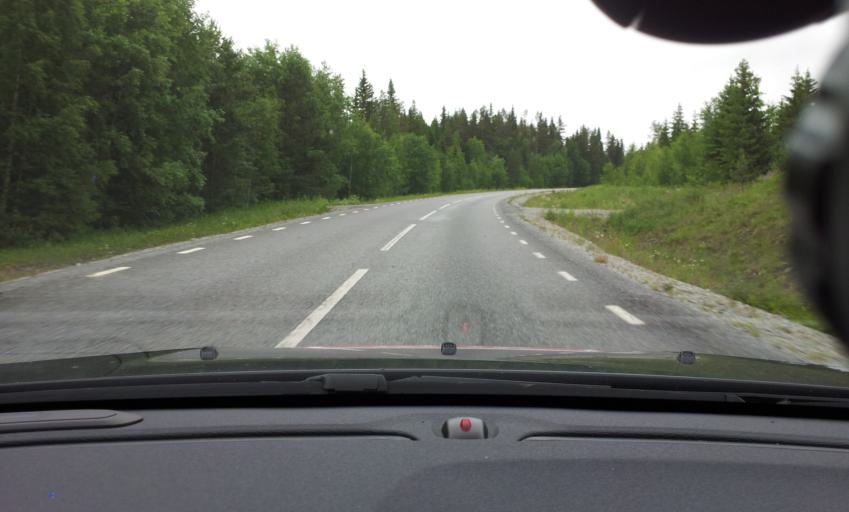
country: SE
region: Jaemtland
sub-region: OEstersunds Kommun
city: Lit
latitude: 63.6856
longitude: 14.6718
